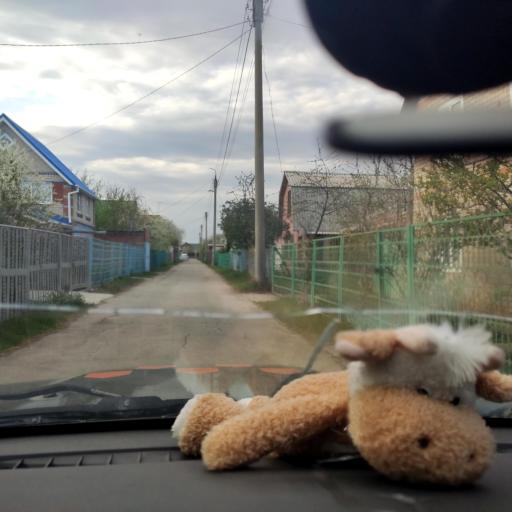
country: RU
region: Samara
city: Podstepki
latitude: 53.5087
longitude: 49.1893
